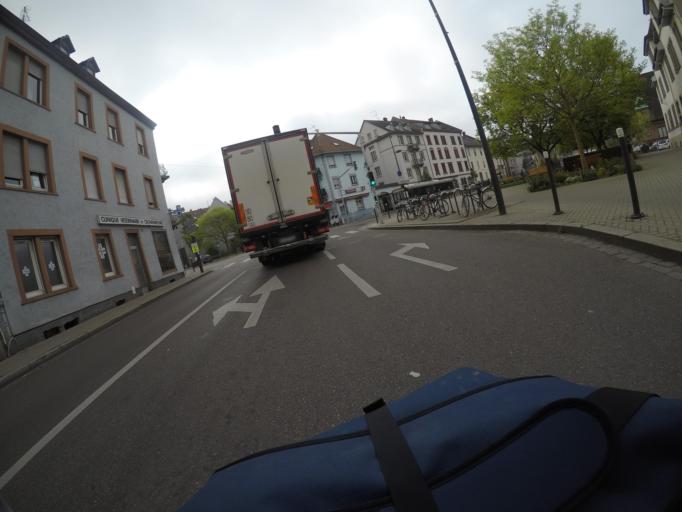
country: FR
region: Alsace
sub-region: Departement du Bas-Rhin
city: Strasbourg
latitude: 48.5955
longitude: 7.7175
